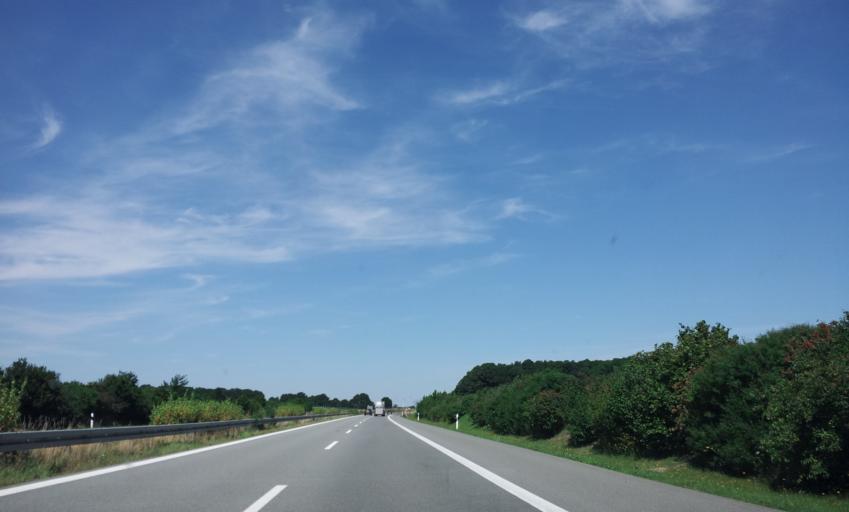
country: DE
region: Mecklenburg-Vorpommern
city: Neuenkirchen
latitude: 53.6195
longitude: 13.3682
